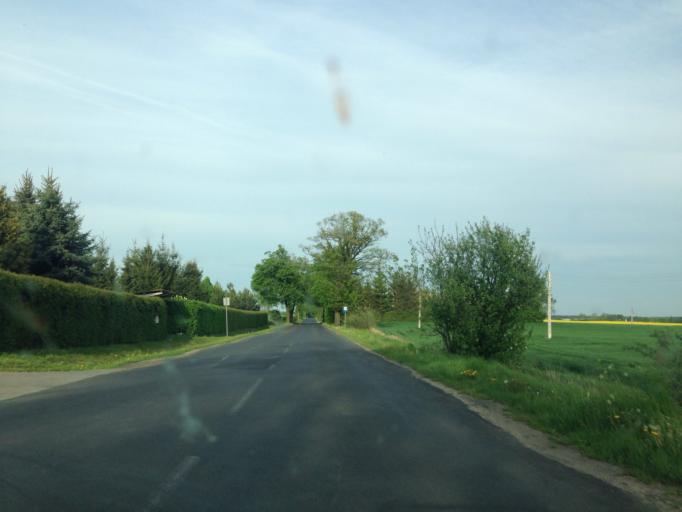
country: PL
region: Kujawsko-Pomorskie
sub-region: Powiat wabrzeski
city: Pluznica
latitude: 53.2881
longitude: 18.8314
